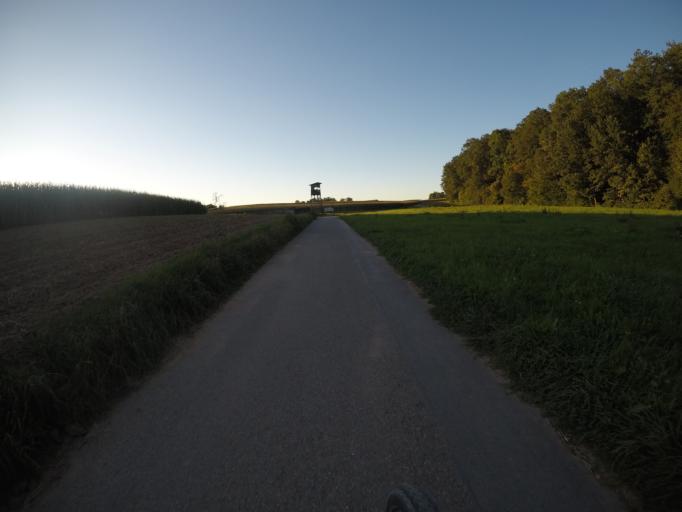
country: DE
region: Baden-Wuerttemberg
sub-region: Regierungsbezirk Stuttgart
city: Steinenbronn
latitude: 48.6954
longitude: 9.1297
